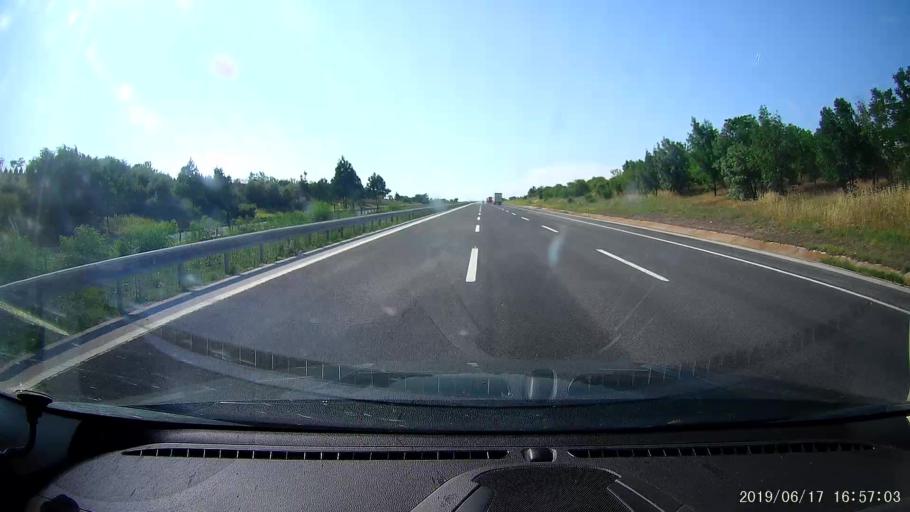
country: TR
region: Edirne
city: Haskoy
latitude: 41.5953
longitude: 26.9226
